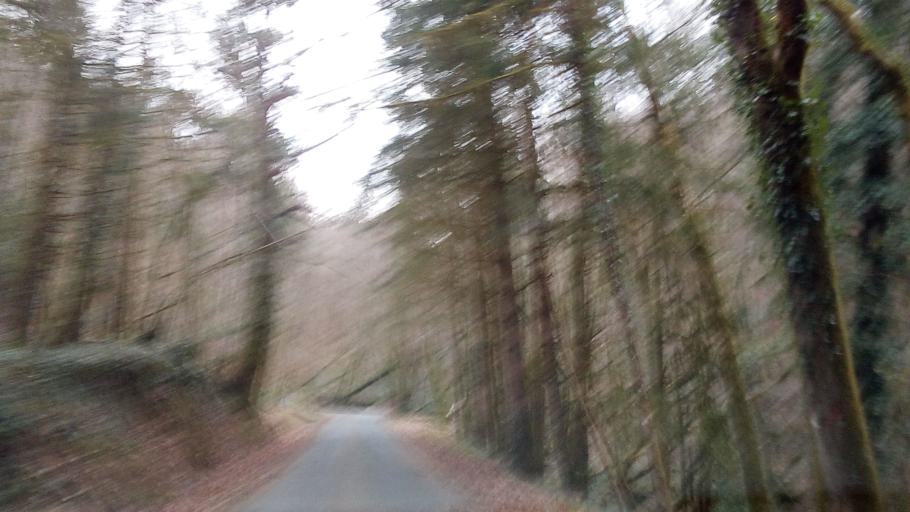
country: FR
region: Limousin
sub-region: Departement de la Correze
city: Naves
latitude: 45.3149
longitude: 1.7780
